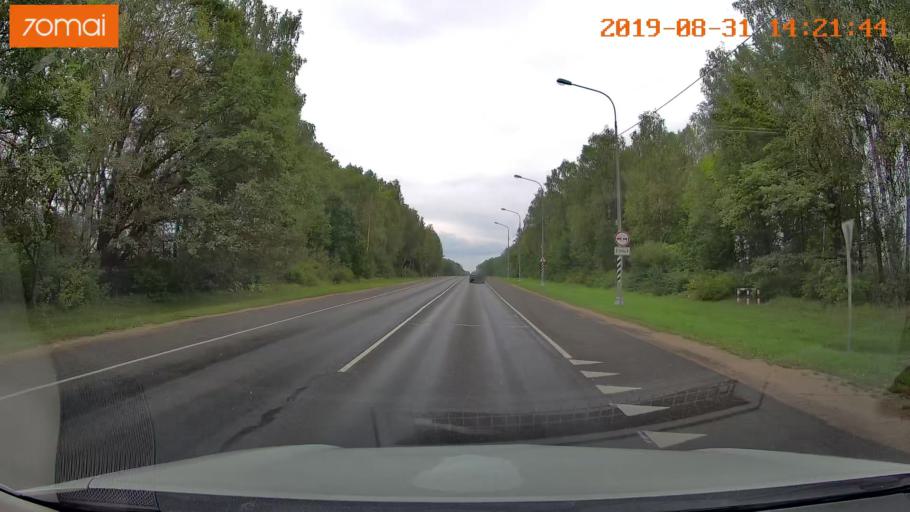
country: RU
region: Smolensk
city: Yekimovichi
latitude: 54.0873
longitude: 33.2033
